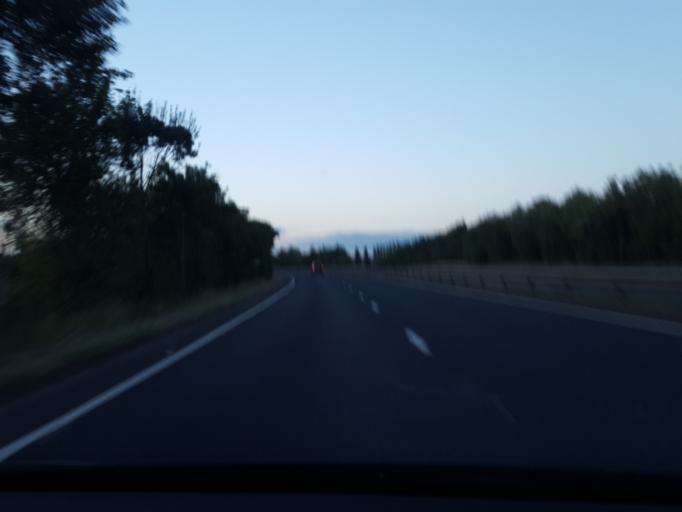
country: GB
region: England
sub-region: Leicestershire
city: Mountsorrel
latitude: 52.7065
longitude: -1.1250
